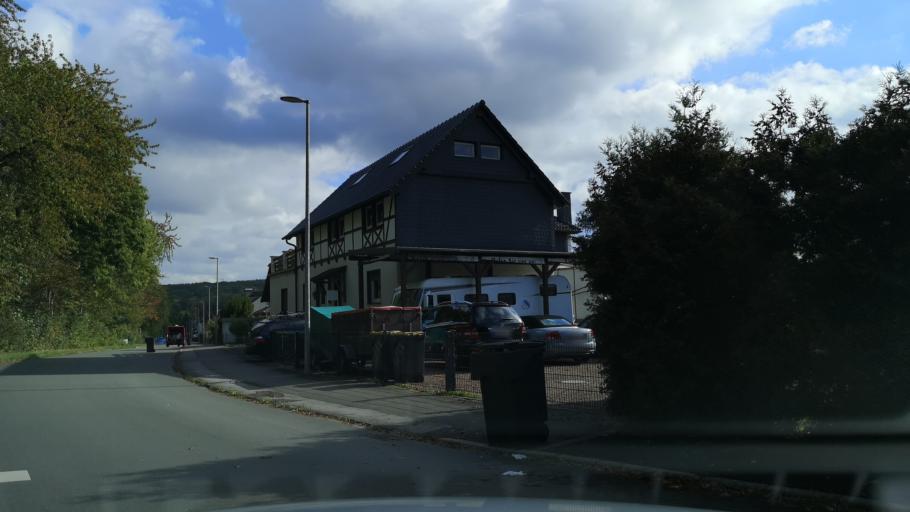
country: DE
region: North Rhine-Westphalia
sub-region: Regierungsbezirk Arnsberg
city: Menden
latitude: 51.4312
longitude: 7.7535
